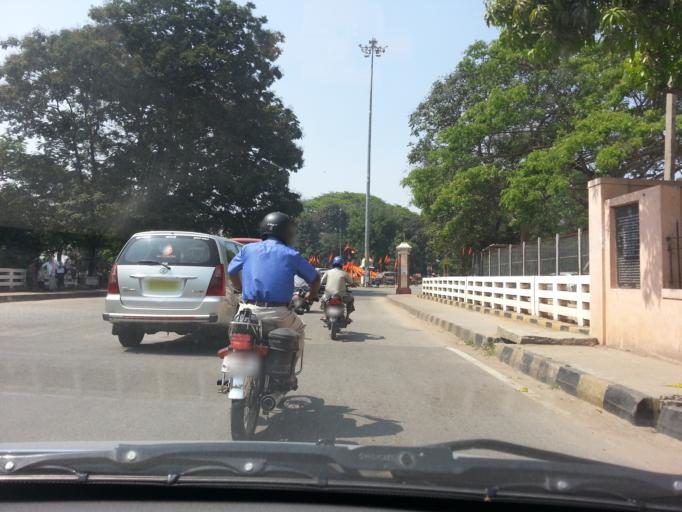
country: IN
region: Karnataka
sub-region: Mysore
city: Mysore
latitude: 12.3078
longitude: 76.6607
